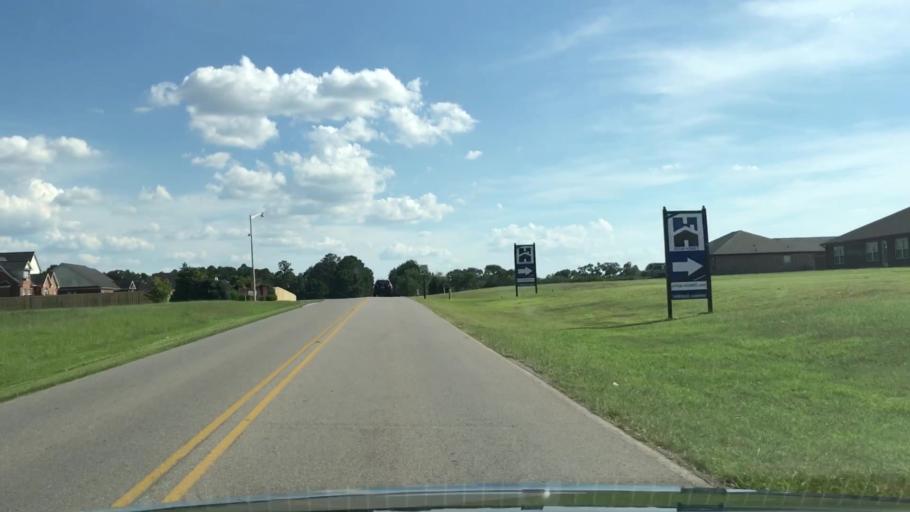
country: US
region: Alabama
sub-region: Madison County
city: Harvest
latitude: 34.8929
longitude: -86.7487
